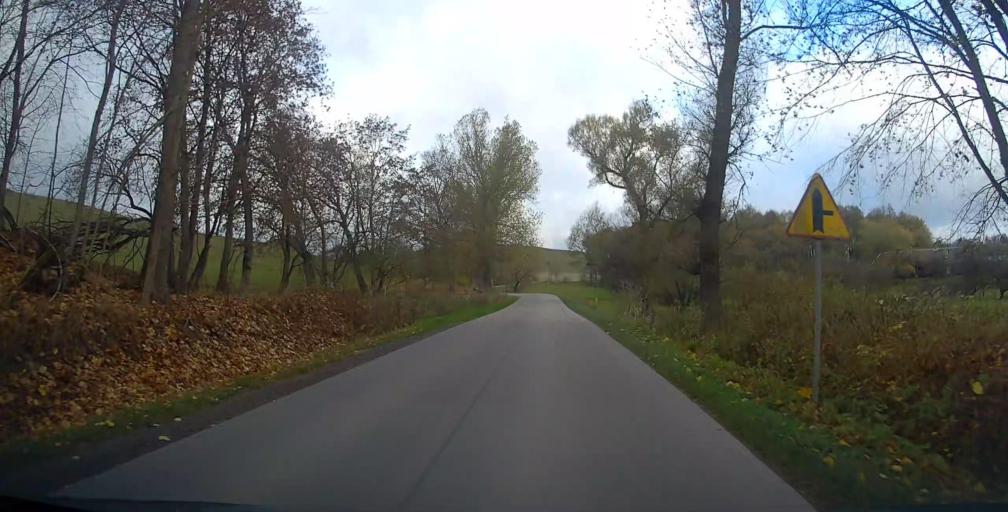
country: PL
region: Podlasie
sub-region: Suwalki
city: Suwalki
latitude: 54.2804
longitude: 22.9082
